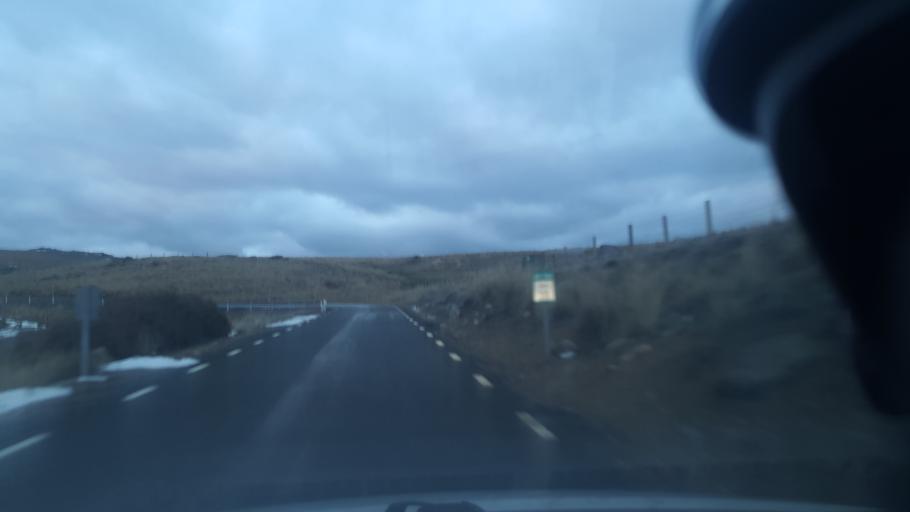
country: ES
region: Castille and Leon
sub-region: Provincia de Avila
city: Ojos-Albos
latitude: 40.7040
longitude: -4.4467
